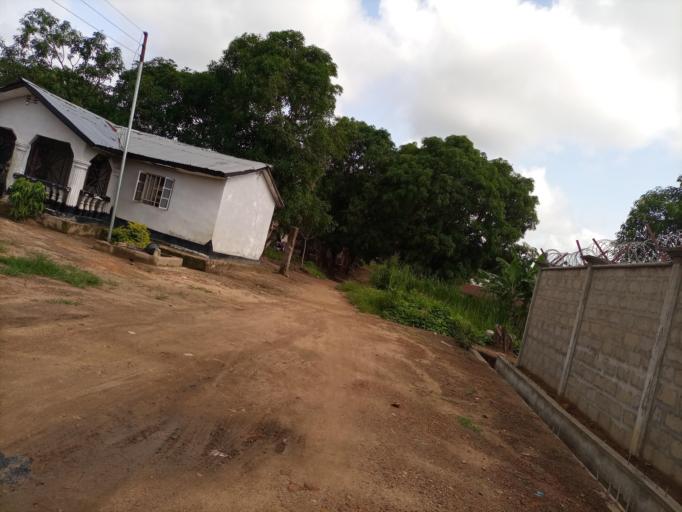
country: SL
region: Southern Province
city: Bo
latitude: 7.9668
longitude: -11.7624
